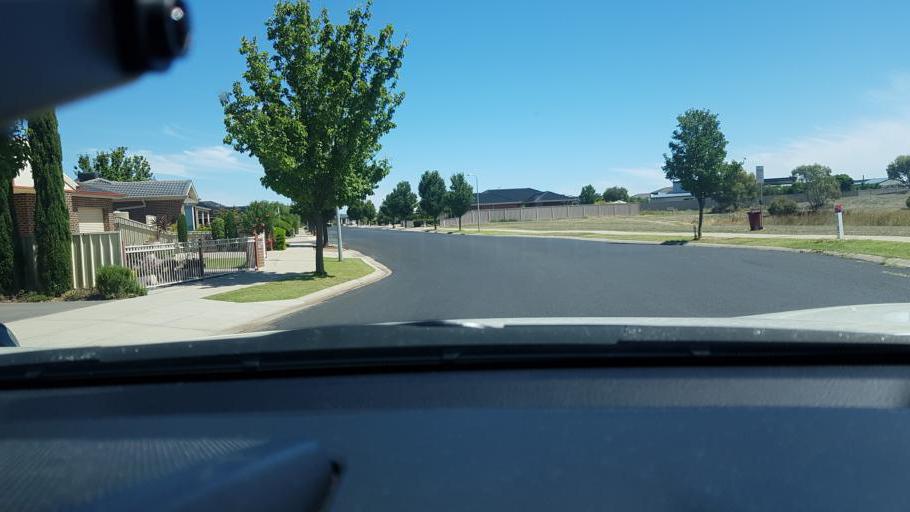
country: AU
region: Victoria
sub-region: Horsham
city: Horsham
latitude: -36.7118
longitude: 142.1821
